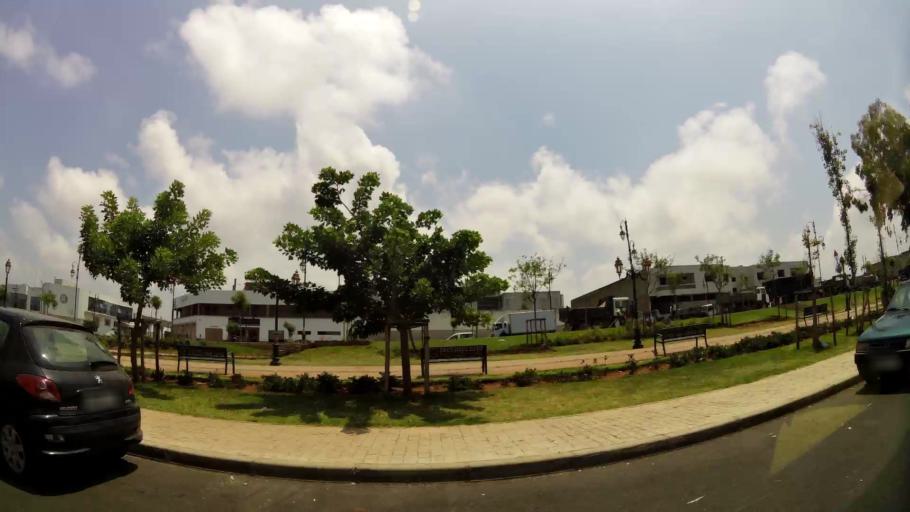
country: MA
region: Rabat-Sale-Zemmour-Zaer
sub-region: Rabat
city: Rabat
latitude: 33.9847
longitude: -6.8755
